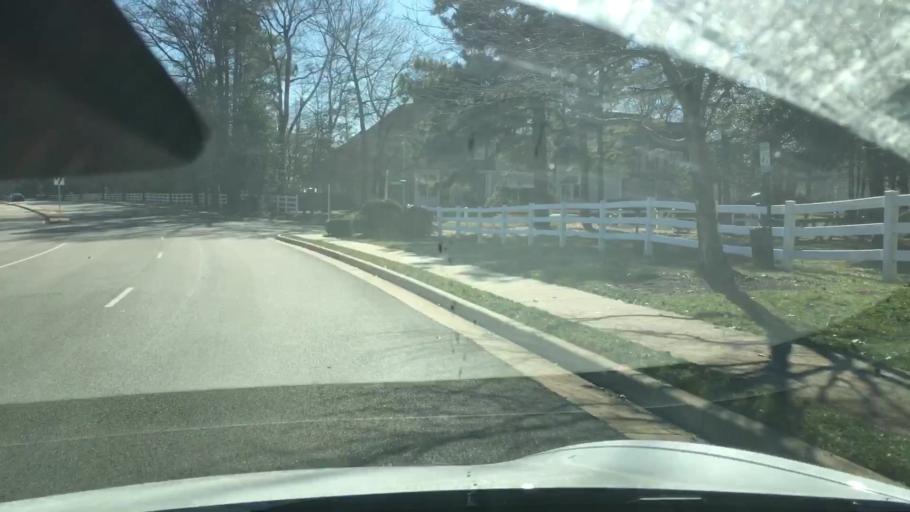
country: US
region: Virginia
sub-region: Henrico County
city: Glen Allen
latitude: 37.6676
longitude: -77.4671
